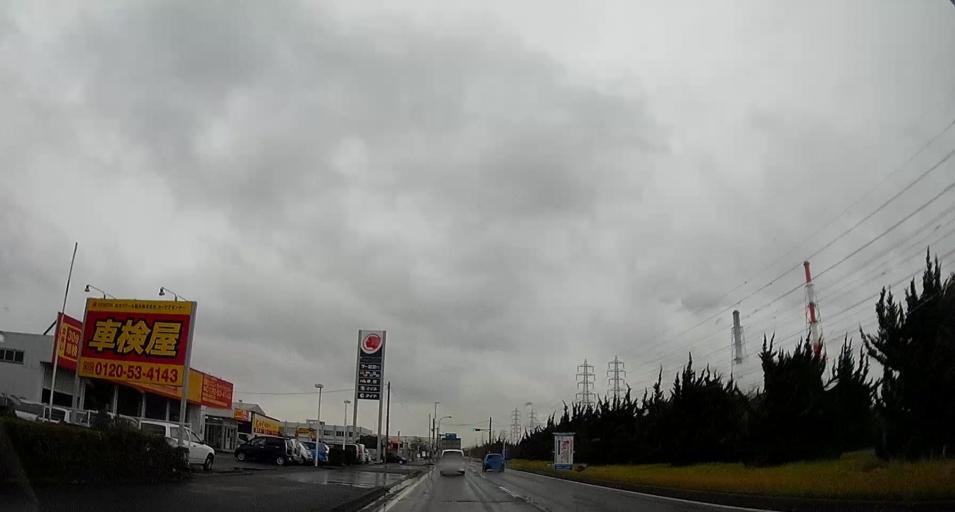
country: JP
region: Chiba
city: Ichihara
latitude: 35.4877
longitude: 140.0414
